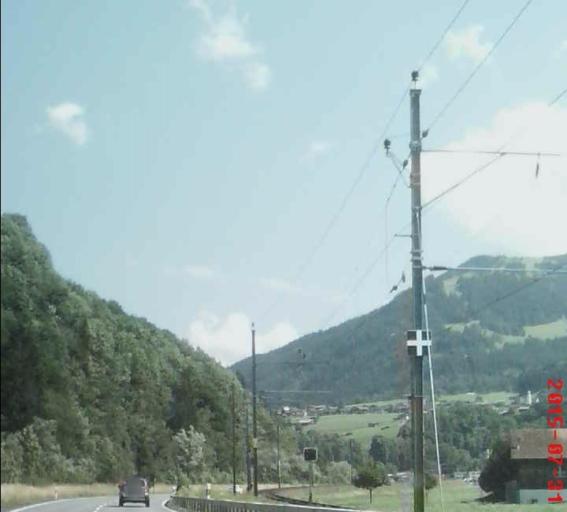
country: CH
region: Grisons
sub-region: Praettigau/Davos District
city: Jenaz
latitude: 46.9296
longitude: 9.7210
